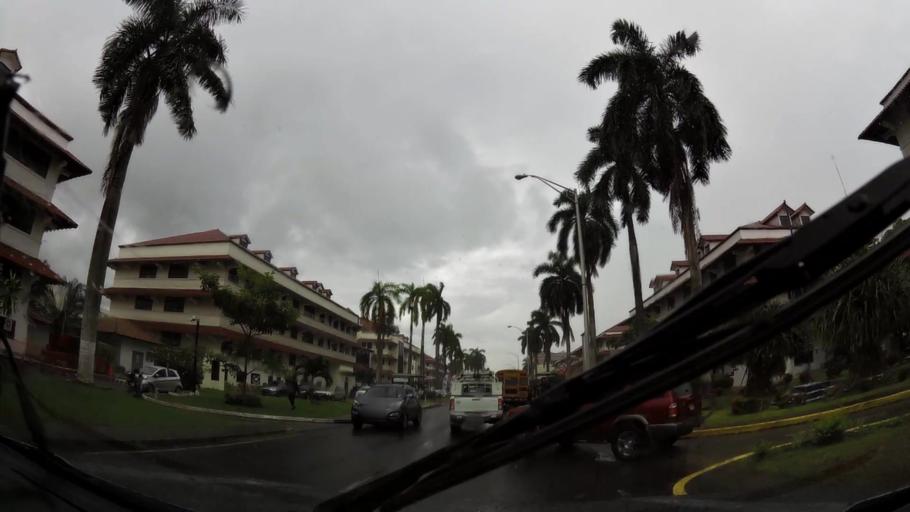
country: PA
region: Panama
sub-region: Distrito de Panama
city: Ancon
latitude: 8.9717
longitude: -79.5630
